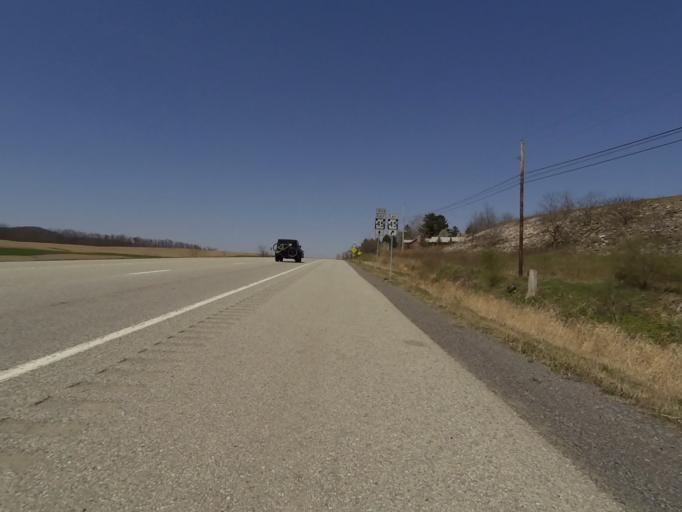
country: US
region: Pennsylvania
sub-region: Blair County
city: Williamsburg
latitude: 40.5792
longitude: -78.1426
